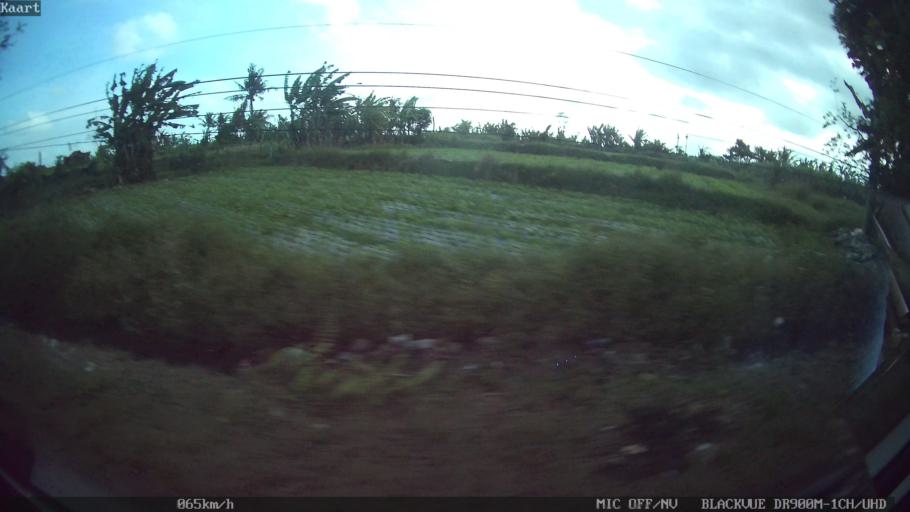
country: ID
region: Bali
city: Banjar Mambalkajanan
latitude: -8.5571
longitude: 115.2329
